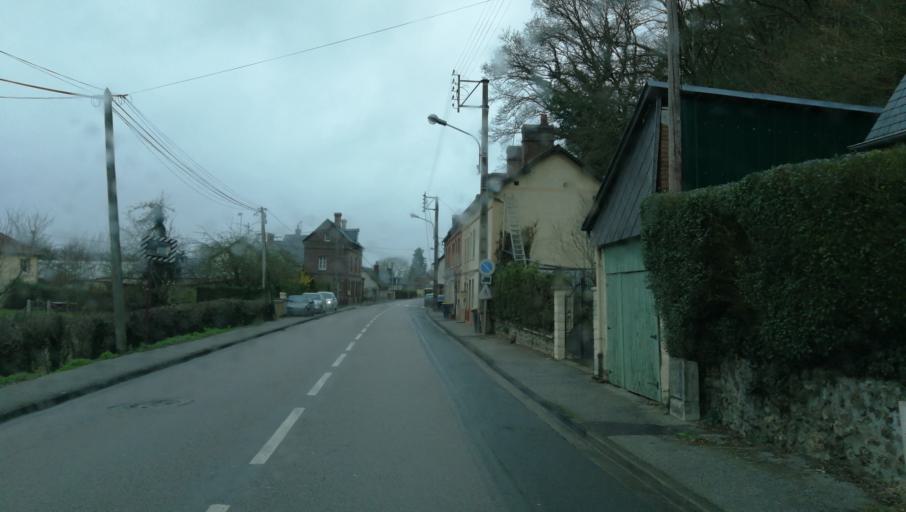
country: FR
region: Haute-Normandie
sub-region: Departement de l'Eure
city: Brionne
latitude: 49.1876
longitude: 0.7240
